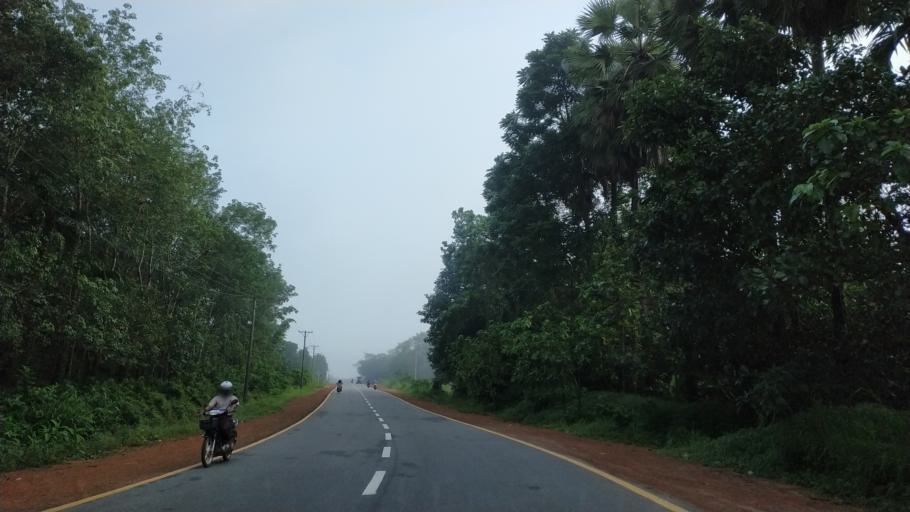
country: MM
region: Tanintharyi
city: Dawei
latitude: 14.2066
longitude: 98.2082
